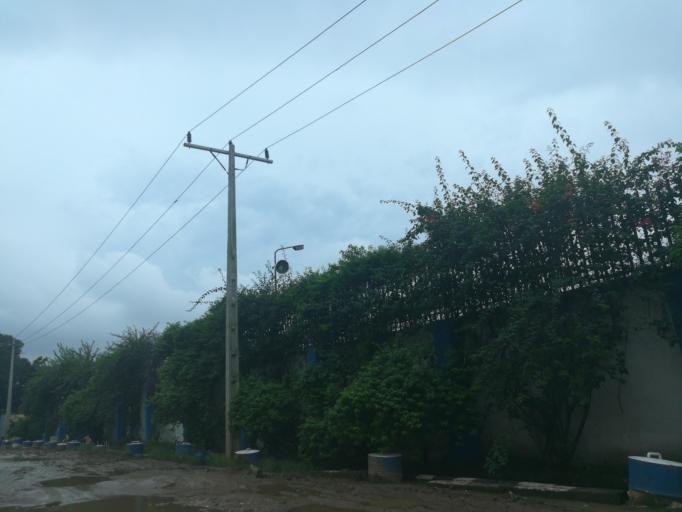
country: NG
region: Lagos
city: Agege
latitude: 6.6131
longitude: 3.3411
